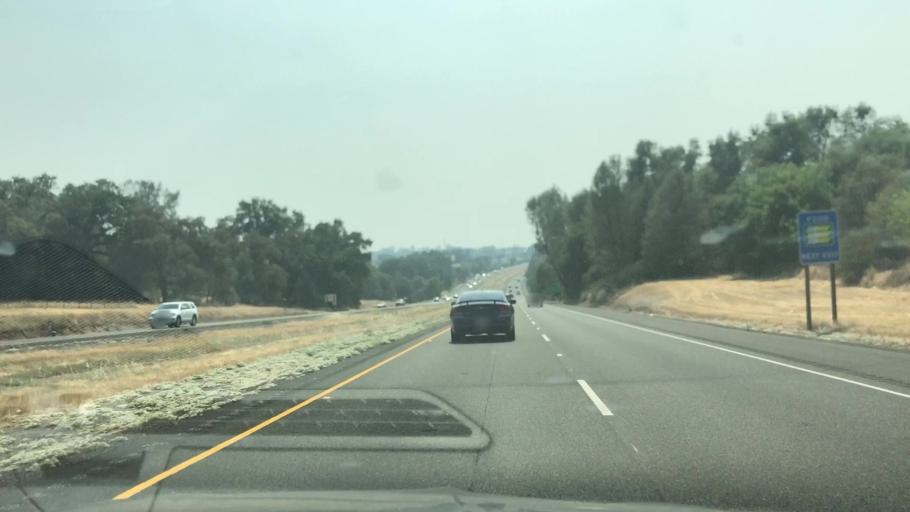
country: US
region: California
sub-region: El Dorado County
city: Shingle Springs
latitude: 38.6724
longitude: -120.9232
